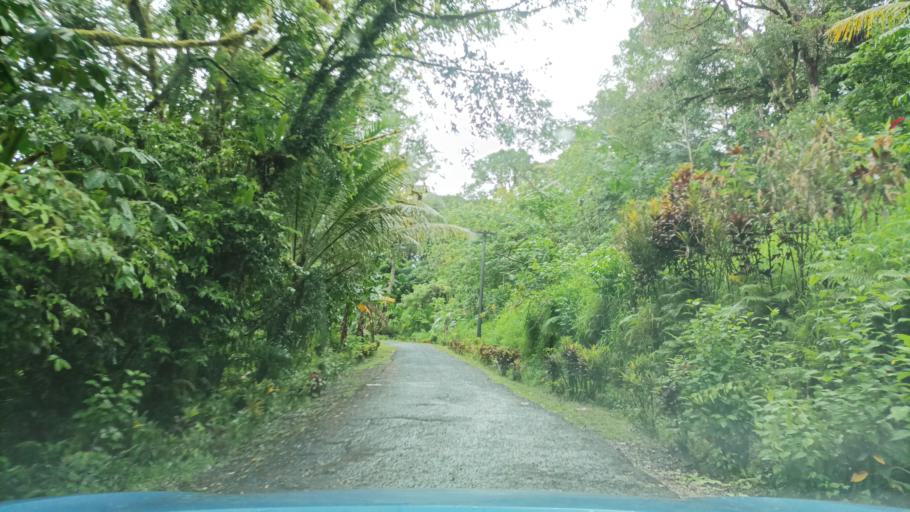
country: FM
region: Pohnpei
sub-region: Sokehs Municipality
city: Palikir - National Government Center
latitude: 6.8274
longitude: 158.1700
